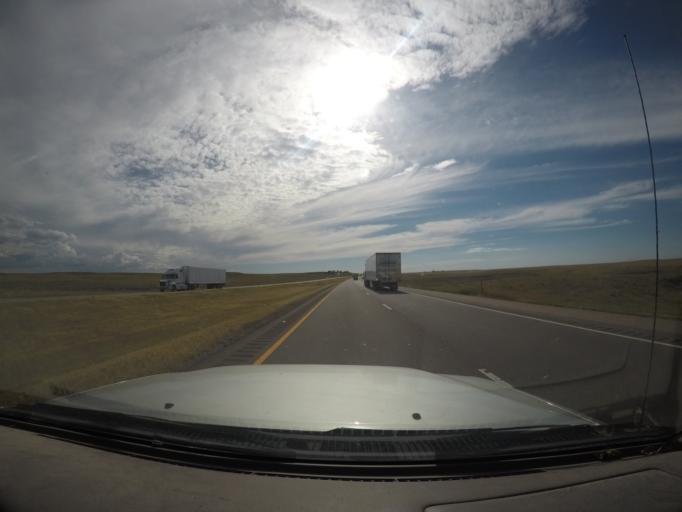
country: US
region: Nebraska
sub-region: Kimball County
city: Kimball
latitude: 41.1908
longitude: -103.8571
